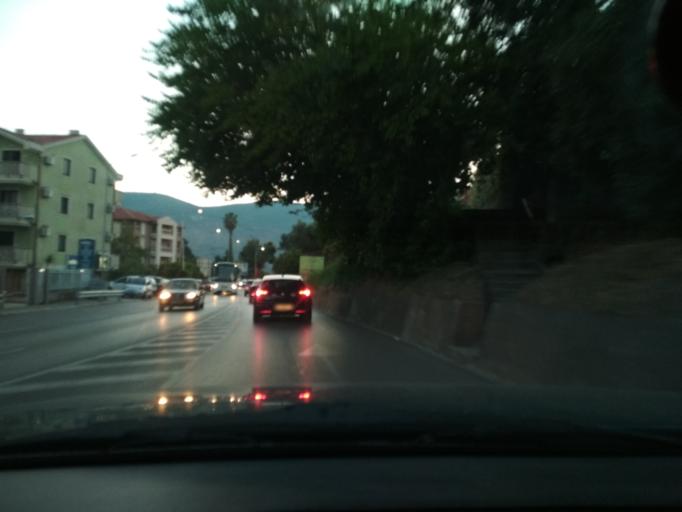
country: ME
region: Herceg Novi
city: Herceg-Novi
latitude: 42.4589
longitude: 18.5254
